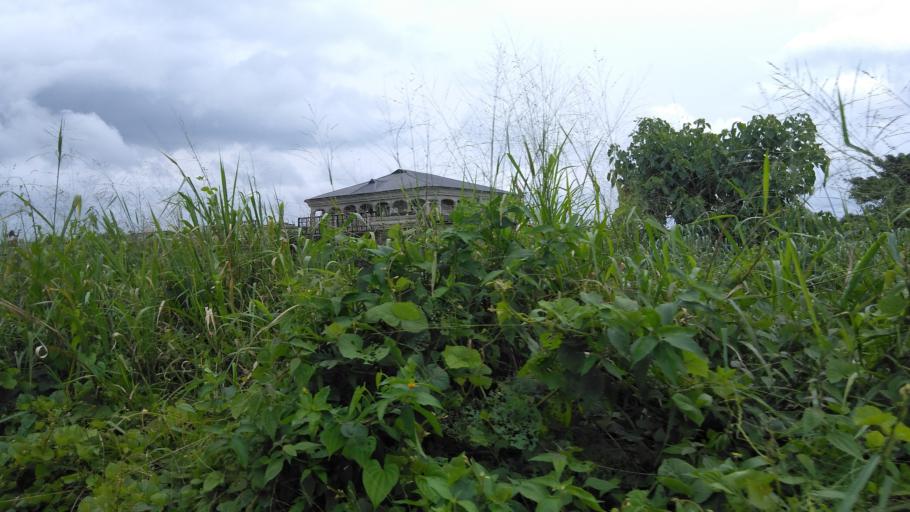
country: NG
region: Ogun
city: Abigi
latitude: 6.6050
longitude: 4.4877
